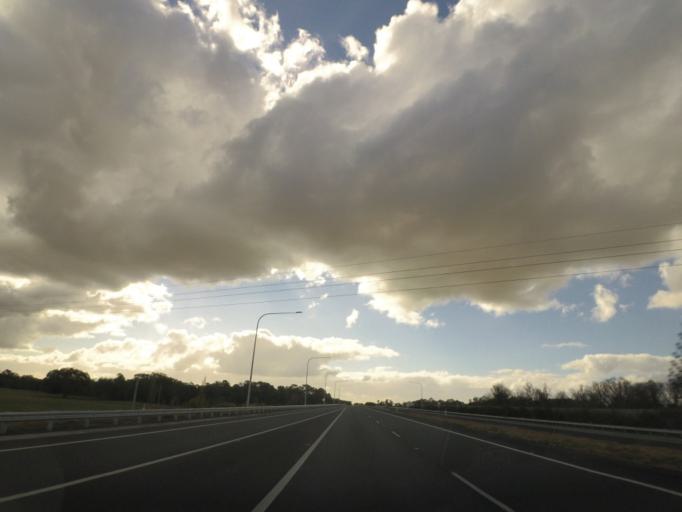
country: AU
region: New South Wales
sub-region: Greater Hume Shire
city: Holbrook
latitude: -35.7289
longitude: 147.3048
